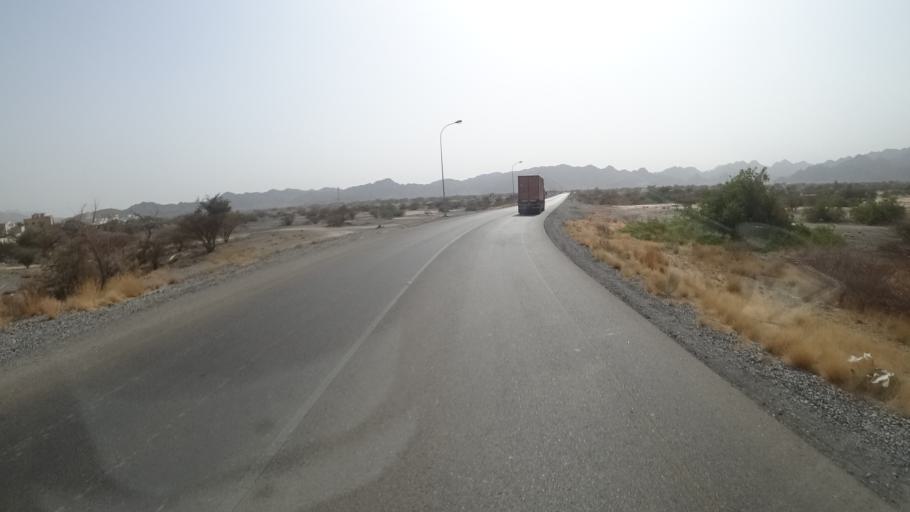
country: OM
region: Muhafazat ad Dakhiliyah
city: Nizwa
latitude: 22.9985
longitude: 57.5501
